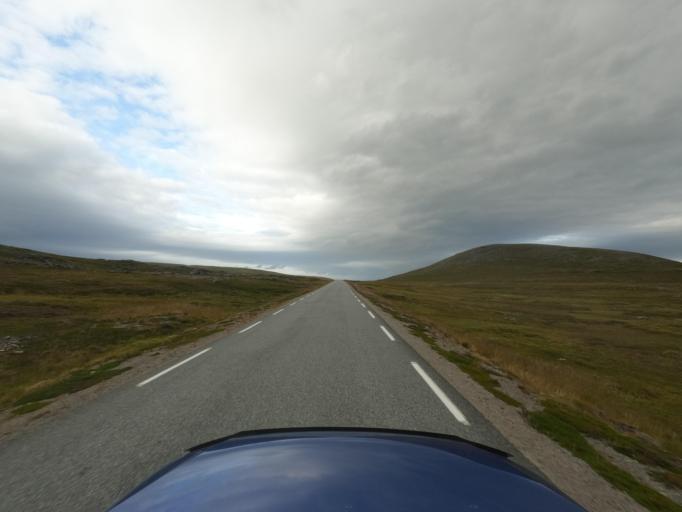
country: NO
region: Finnmark Fylke
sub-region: Nordkapp
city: Honningsvag
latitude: 70.8471
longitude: 25.7944
